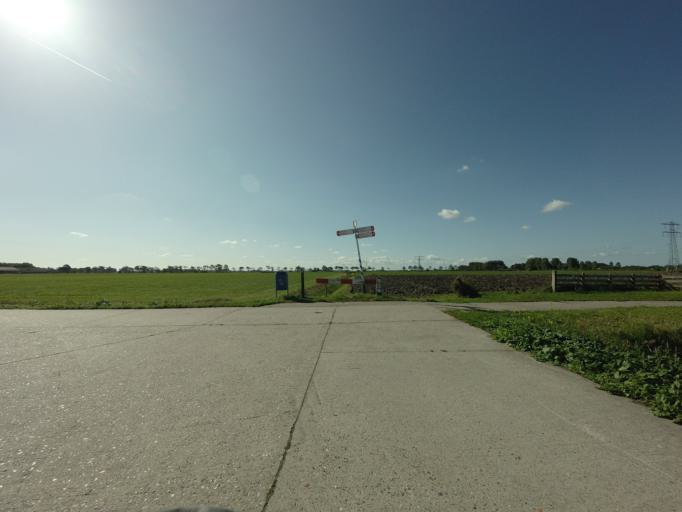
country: NL
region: Friesland
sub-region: Gemeente Leeuwarden
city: Wirdum
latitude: 53.1532
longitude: 5.7703
